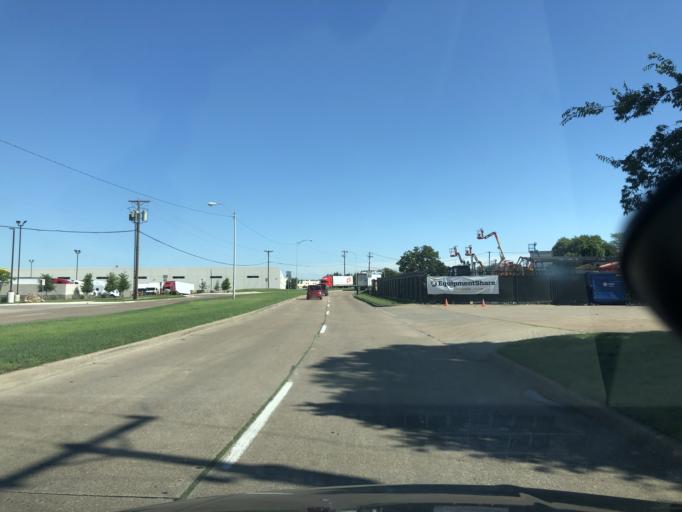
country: US
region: Texas
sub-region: Tarrant County
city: Euless
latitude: 32.8015
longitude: -97.0294
